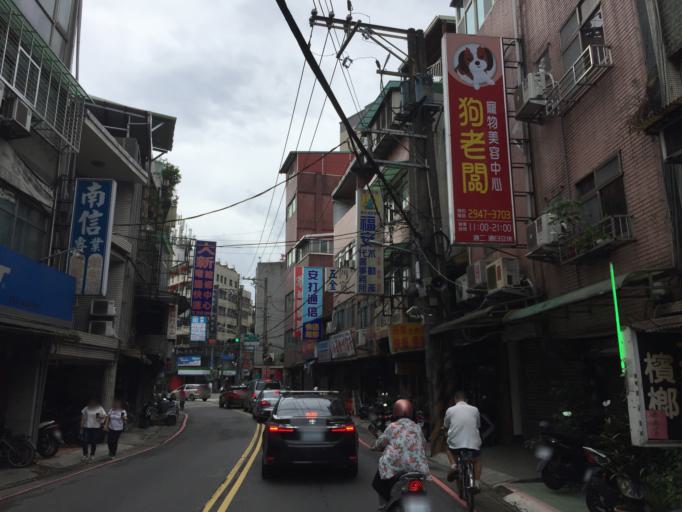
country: TW
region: Taipei
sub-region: Taipei
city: Banqiao
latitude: 24.9872
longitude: 121.5079
